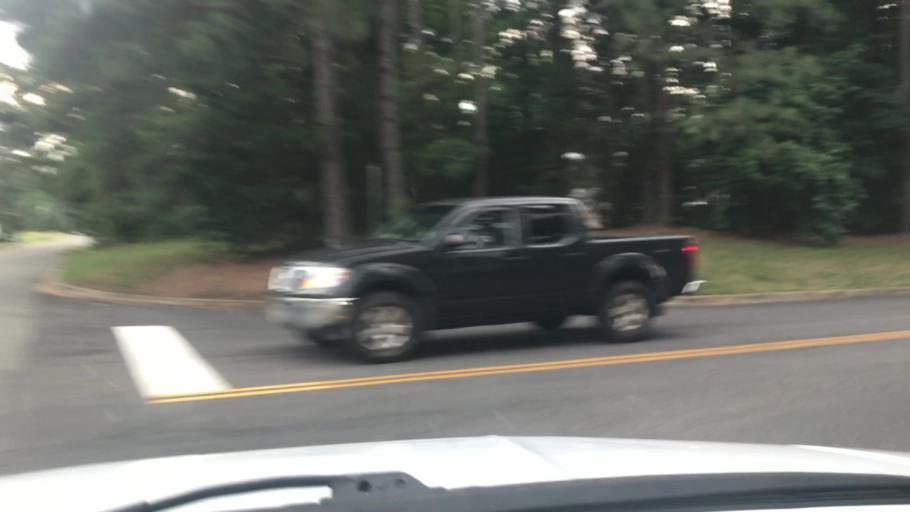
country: US
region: Virginia
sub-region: Henrico County
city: Tuckahoe
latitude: 37.6004
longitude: -77.5827
